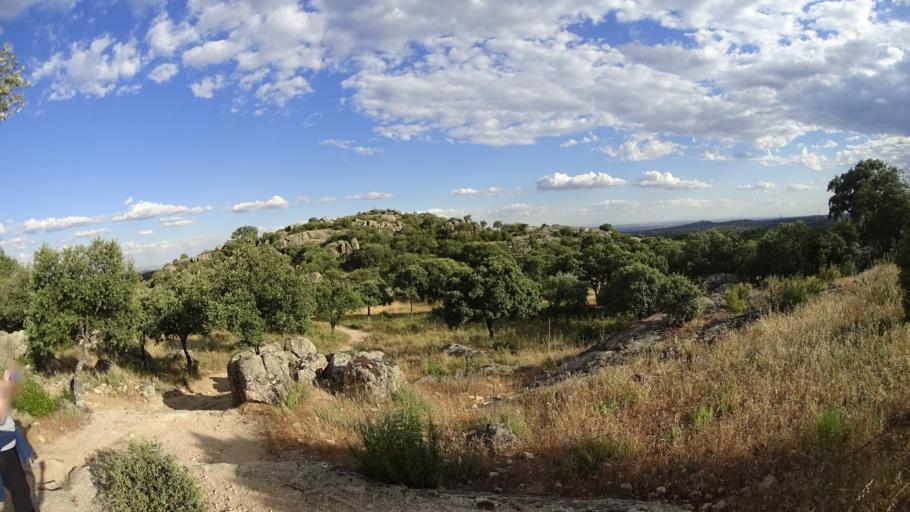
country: ES
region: Madrid
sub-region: Provincia de Madrid
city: Hoyo de Manzanares
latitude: 40.6343
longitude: -3.9001
